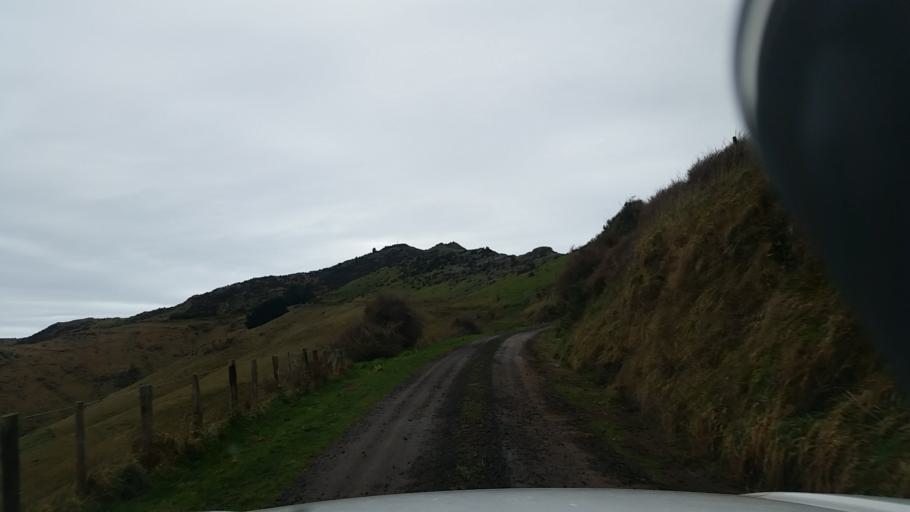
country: NZ
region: Canterbury
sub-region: Christchurch City
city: Christchurch
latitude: -43.7442
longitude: 173.0018
